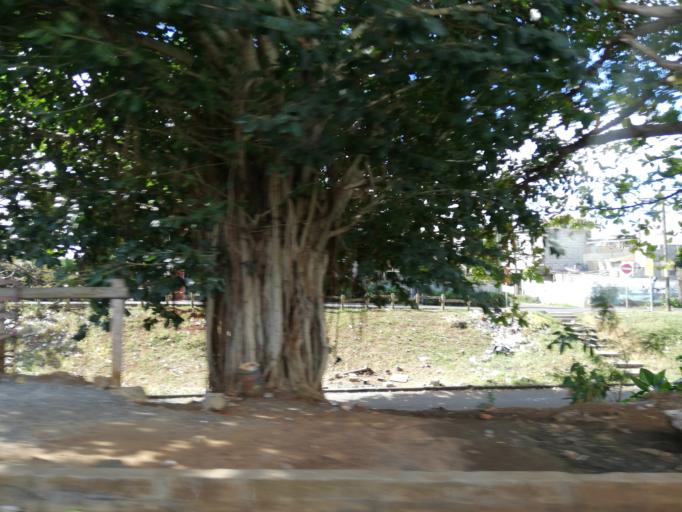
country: MU
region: Black River
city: Petite Riviere
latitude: -20.2220
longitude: 57.4581
